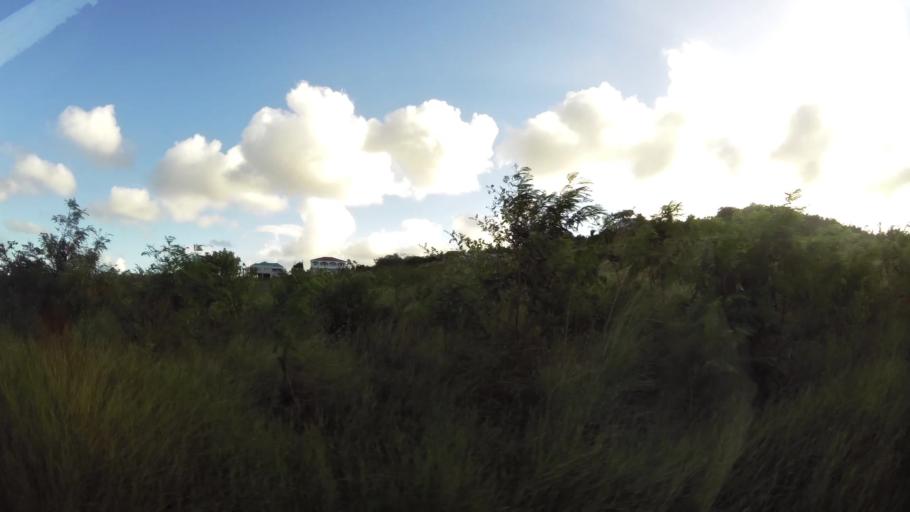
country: AG
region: Saint George
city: Piggotts
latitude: 17.1182
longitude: -61.7922
